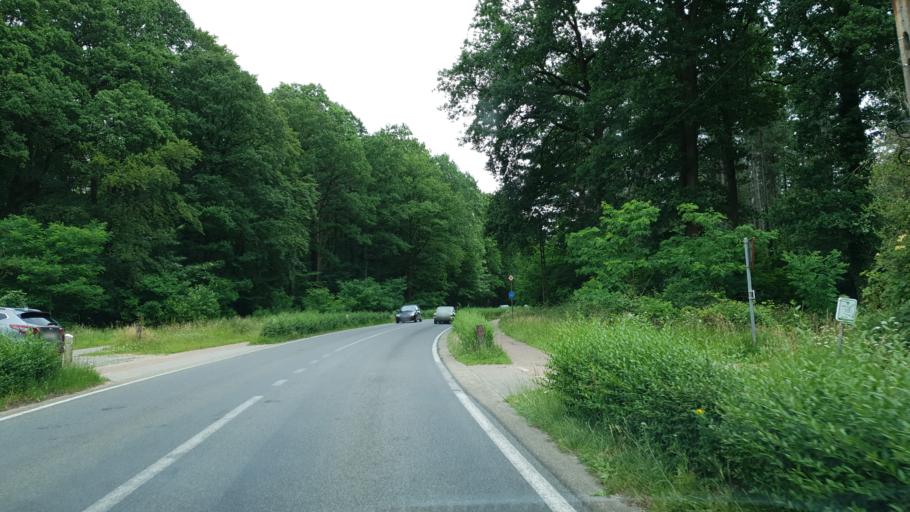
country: BE
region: Flanders
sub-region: Provincie Vlaams-Brabant
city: Scherpenheuvel-Zichem
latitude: 51.0370
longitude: 4.9712
